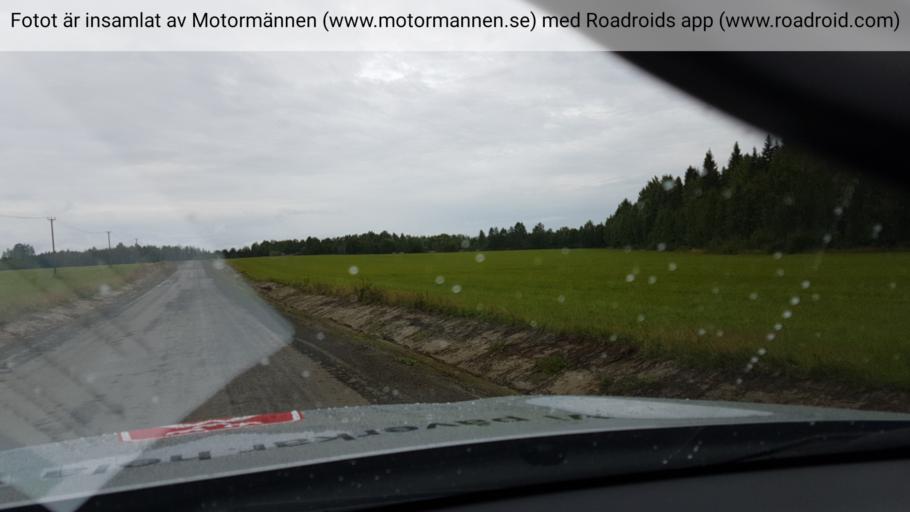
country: SE
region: Norrbotten
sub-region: Alvsbyns Kommun
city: AElvsbyn
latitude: 65.9075
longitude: 21.2989
